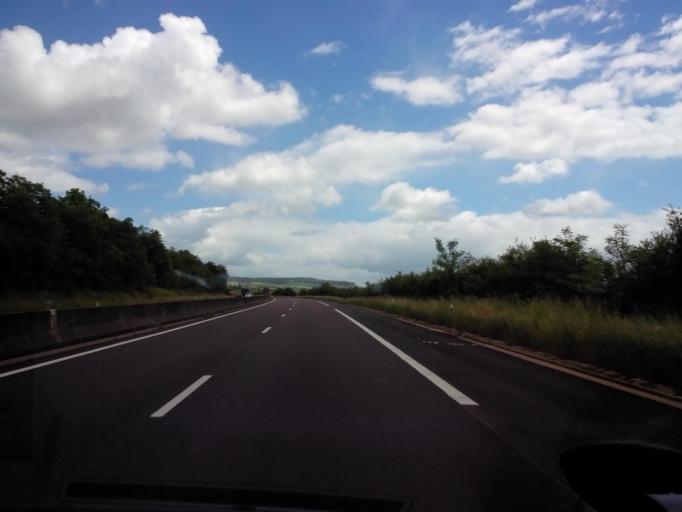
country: FR
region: Champagne-Ardenne
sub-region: Departement de la Haute-Marne
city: Rolampont
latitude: 47.9478
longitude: 5.3412
